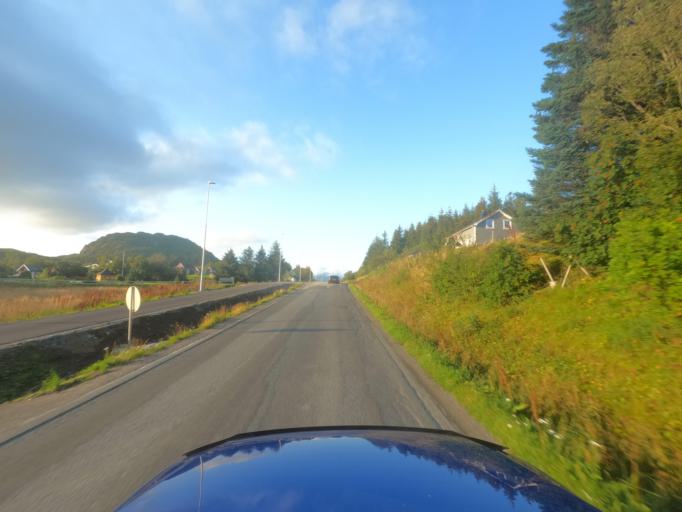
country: NO
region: Nordland
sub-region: Vestvagoy
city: Gravdal
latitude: 68.1012
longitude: 13.5476
